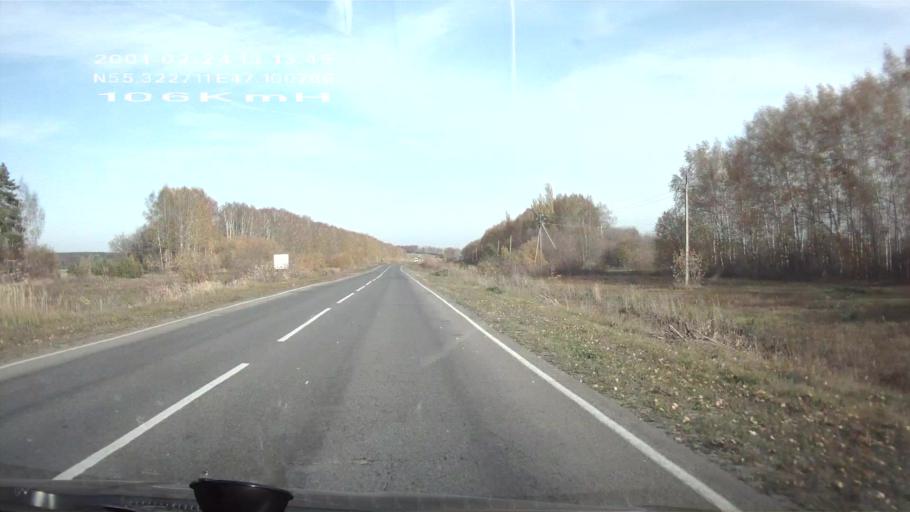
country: RU
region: Chuvashia
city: Ibresi
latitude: 55.3227
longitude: 47.1008
